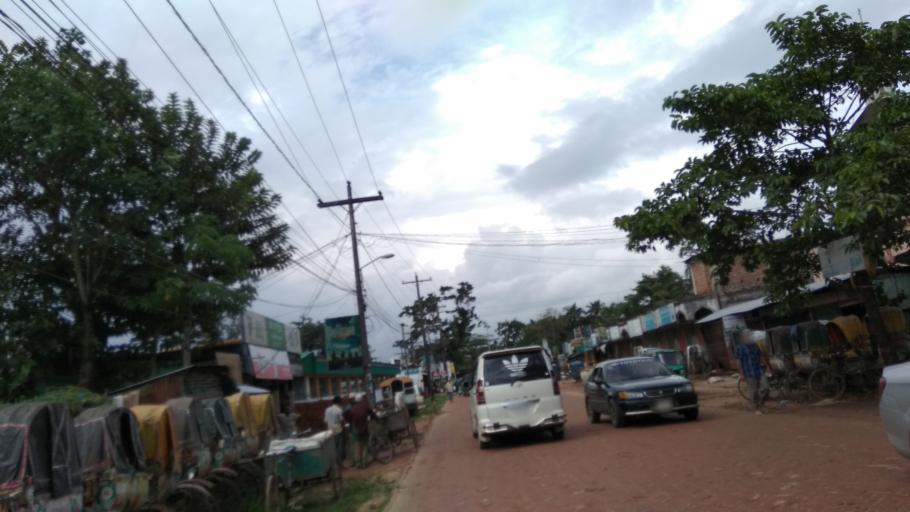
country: IN
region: Tripura
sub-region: Dhalai
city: Kamalpur
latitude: 24.3067
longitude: 91.7383
